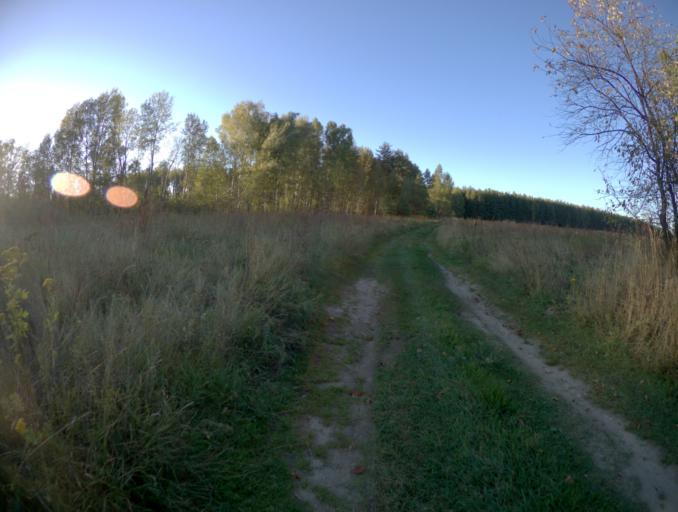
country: RU
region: Vladimir
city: Raduzhnyy
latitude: 56.0067
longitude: 40.2978
